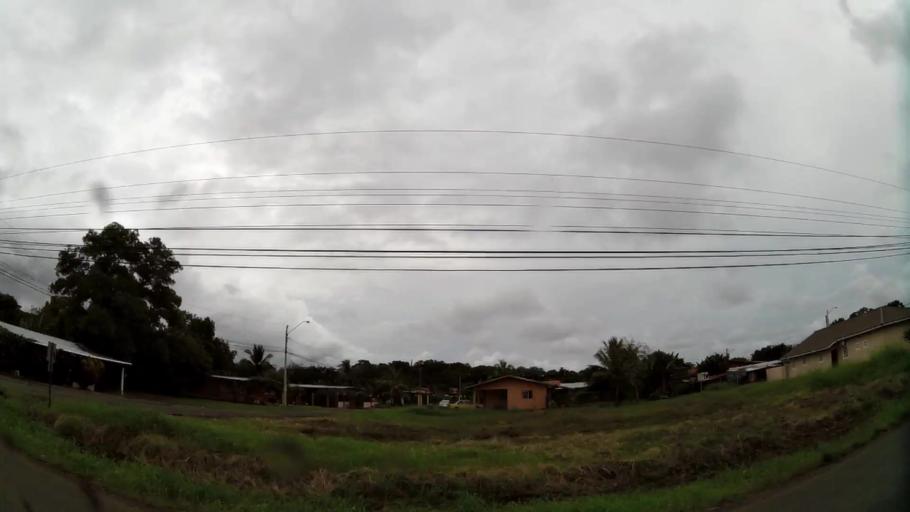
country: PA
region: Chiriqui
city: David
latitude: 8.4004
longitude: -82.4592
